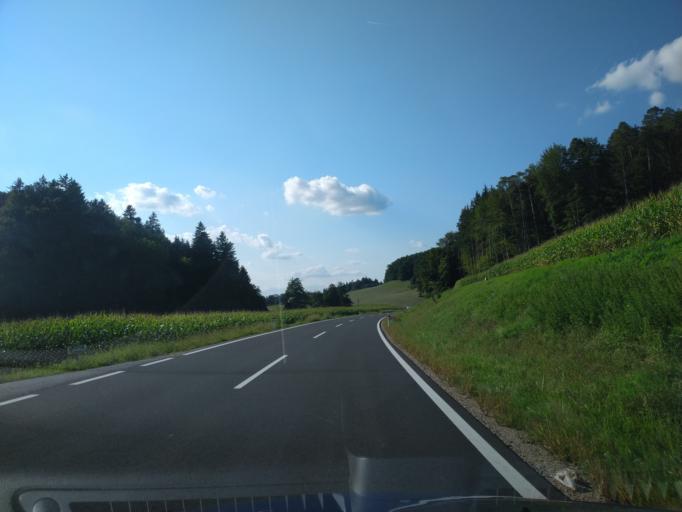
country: AT
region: Styria
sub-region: Politischer Bezirk Leibnitz
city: Gleinstatten
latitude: 46.7355
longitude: 15.3780
